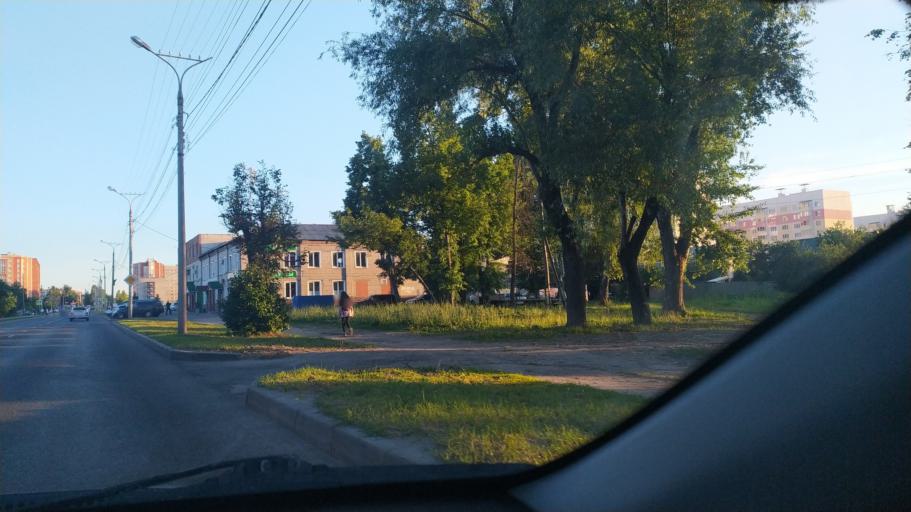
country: RU
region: Chuvashia
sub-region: Cheboksarskiy Rayon
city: Cheboksary
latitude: 56.1193
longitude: 47.2249
